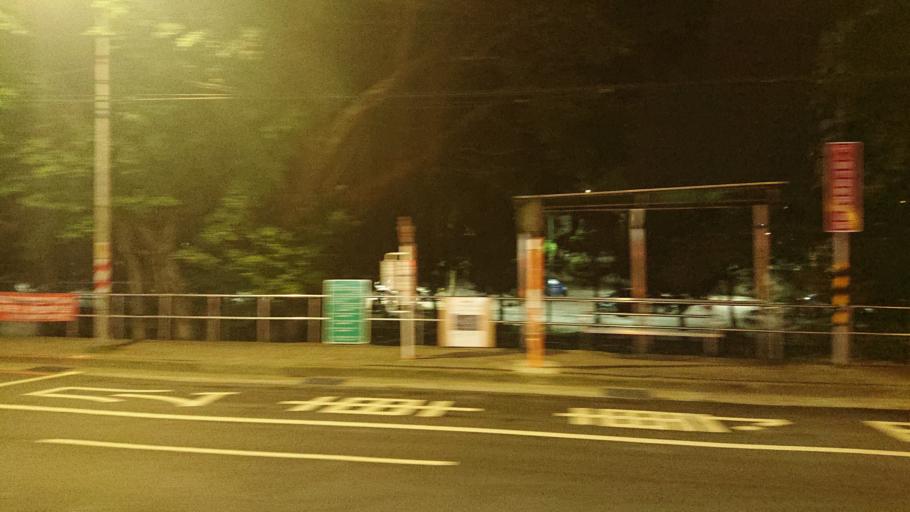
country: TW
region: Taipei
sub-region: Taipei
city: Banqiao
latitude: 24.9534
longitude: 121.4120
